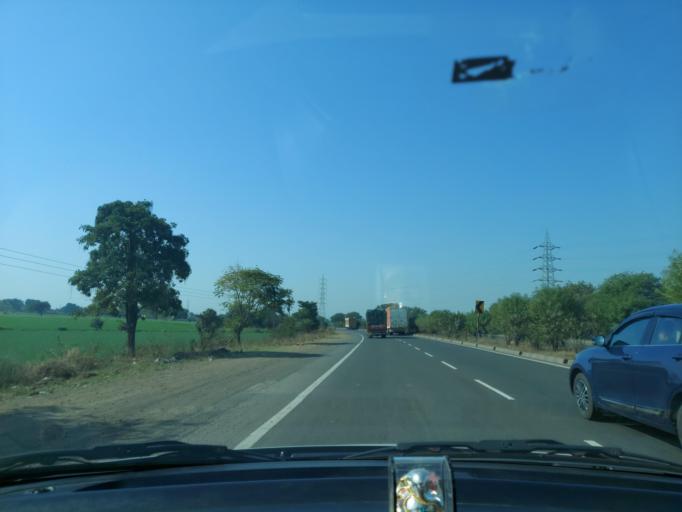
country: IN
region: Madhya Pradesh
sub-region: Indore
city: Pithampur
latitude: 22.5788
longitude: 75.6491
